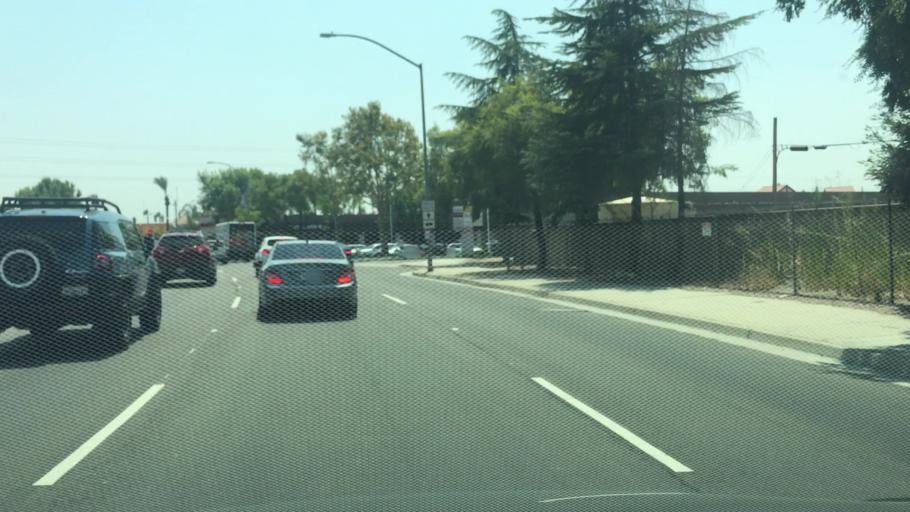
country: US
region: California
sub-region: Fresno County
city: Clovis
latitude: 36.8533
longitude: -119.7908
